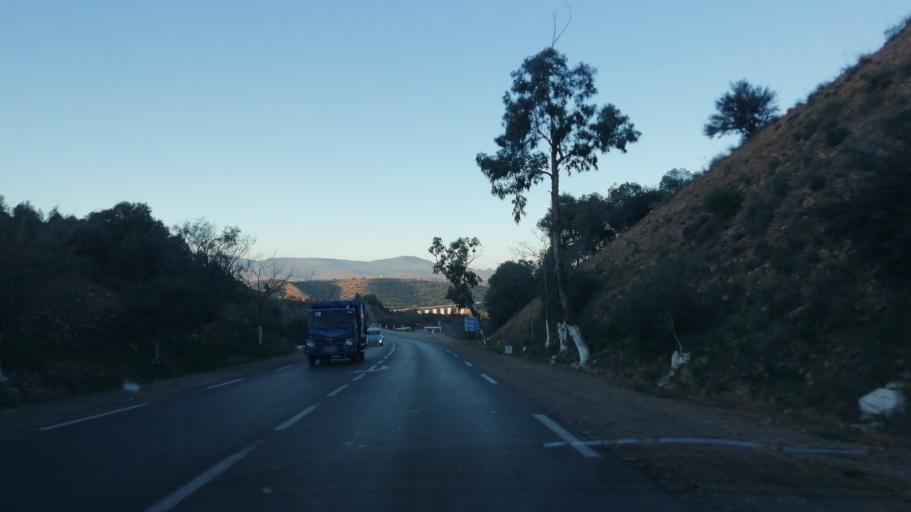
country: DZ
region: Tlemcen
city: Nedroma
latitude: 34.8774
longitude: -1.6684
